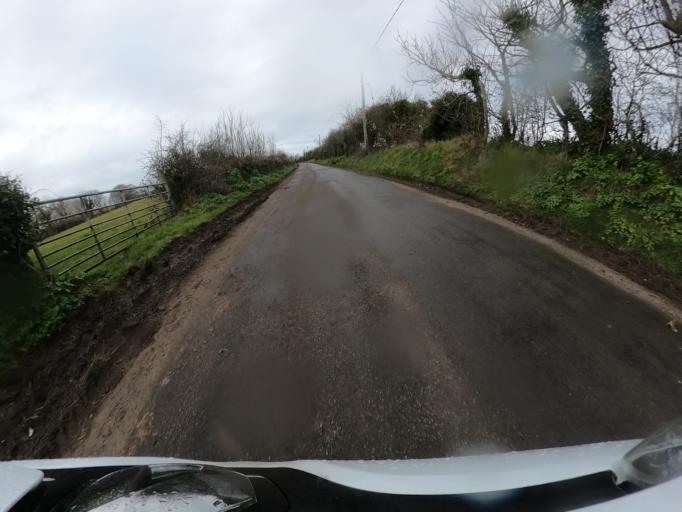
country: IM
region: Ramsey
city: Ramsey
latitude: 54.3782
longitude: -4.4544
